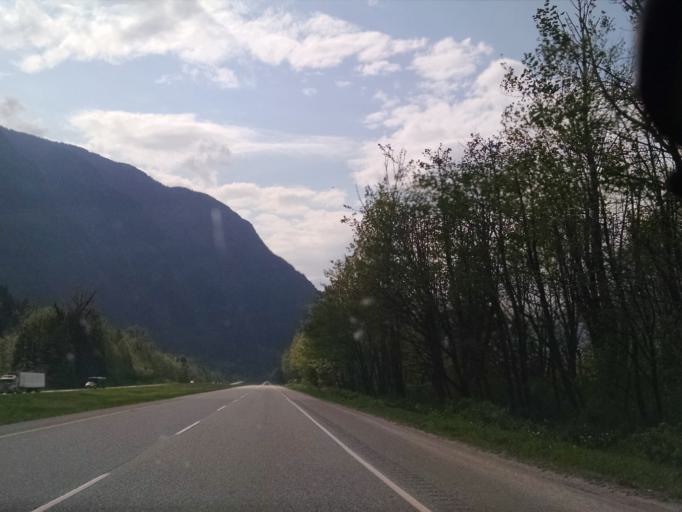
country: CA
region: British Columbia
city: Hope
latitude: 49.3644
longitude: -121.4899
